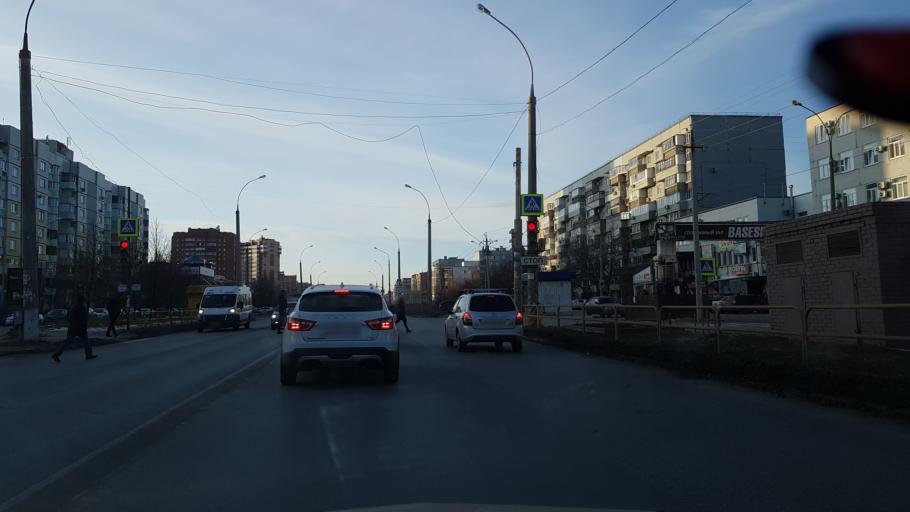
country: RU
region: Samara
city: Tol'yatti
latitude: 53.5408
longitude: 49.3495
